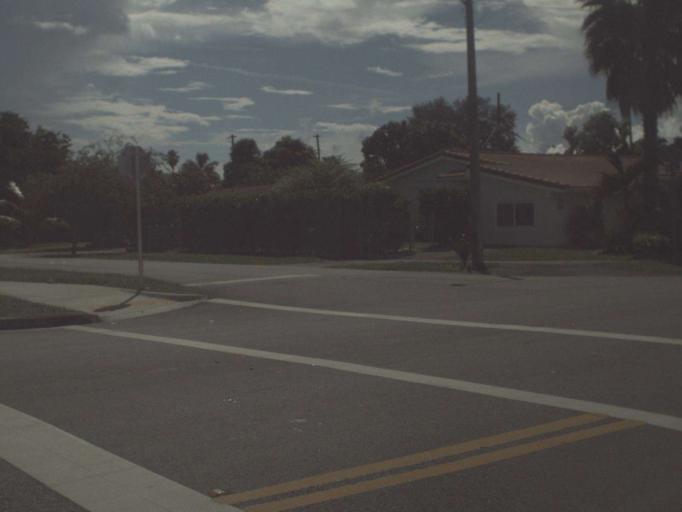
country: US
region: Florida
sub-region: Miami-Dade County
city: Sunset
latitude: 25.7015
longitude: -80.3531
